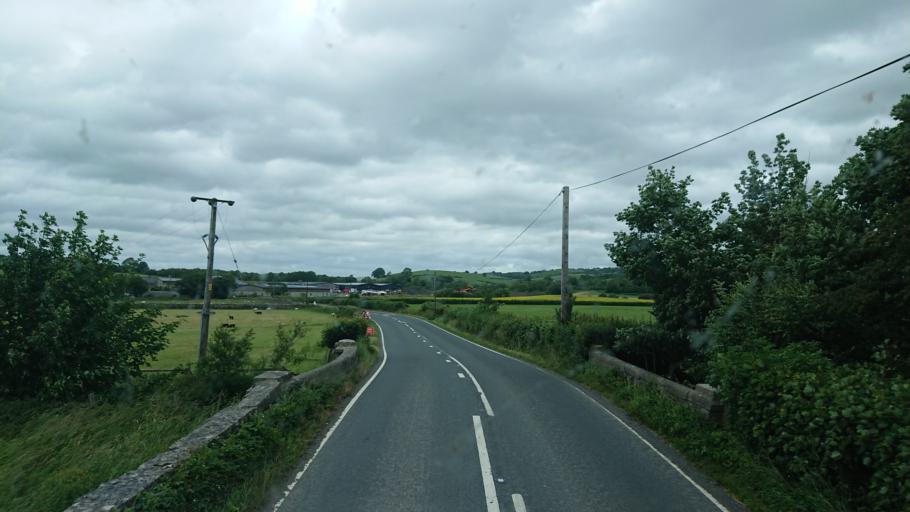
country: GB
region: England
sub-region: Cumbria
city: Milnthorpe
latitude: 54.2292
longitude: -2.7142
